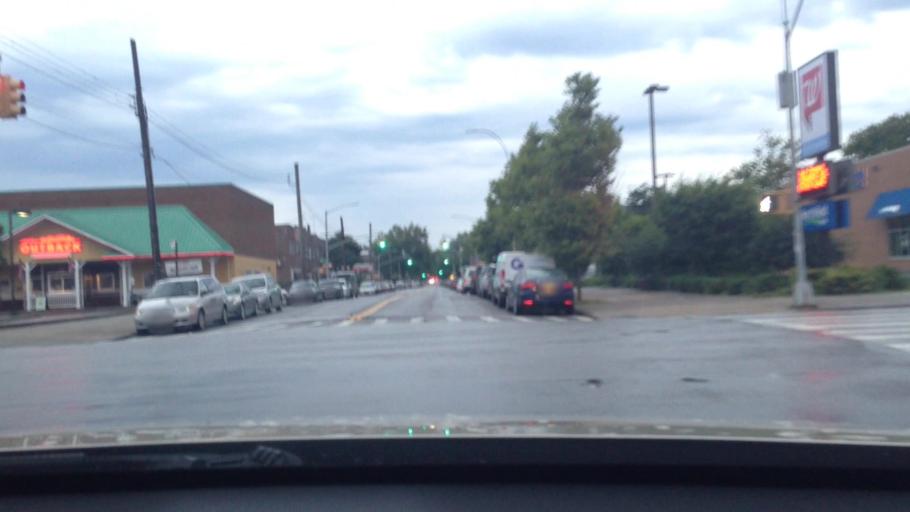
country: US
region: New York
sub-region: Kings County
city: Bensonhurst
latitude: 40.6113
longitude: -74.0096
